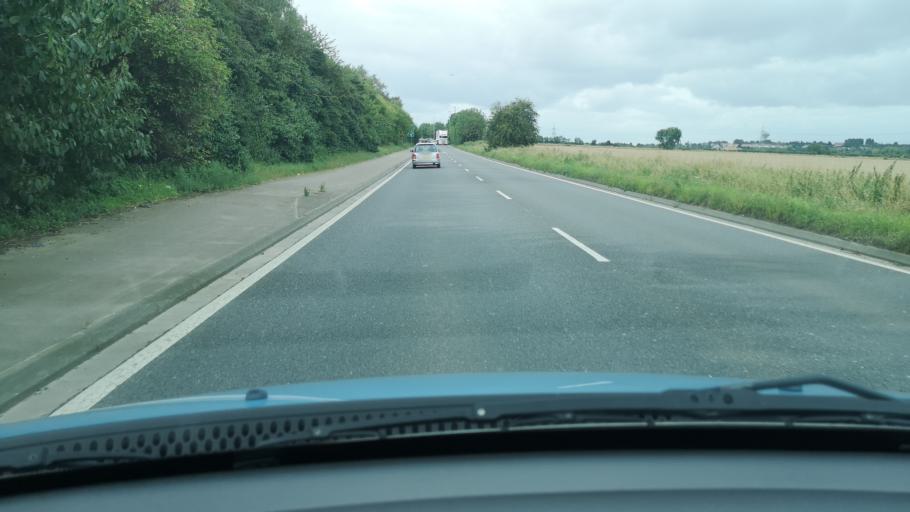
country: GB
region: England
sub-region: City and Borough of Wakefield
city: South Elmsall
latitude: 53.6036
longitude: -1.2667
